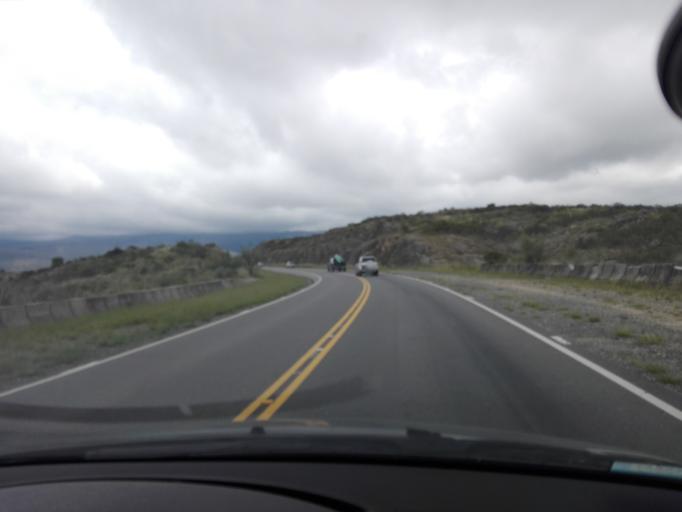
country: AR
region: Cordoba
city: Cuesta Blanca
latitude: -31.5708
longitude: -64.6505
